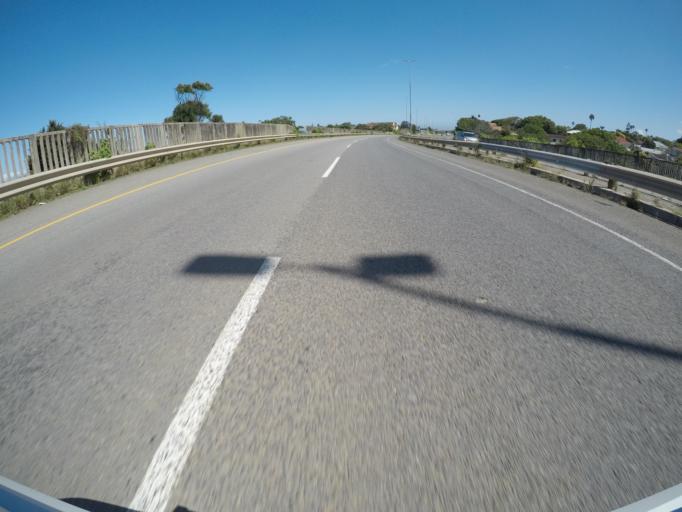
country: ZA
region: Eastern Cape
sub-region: Buffalo City Metropolitan Municipality
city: East London
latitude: -32.9888
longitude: 27.9195
